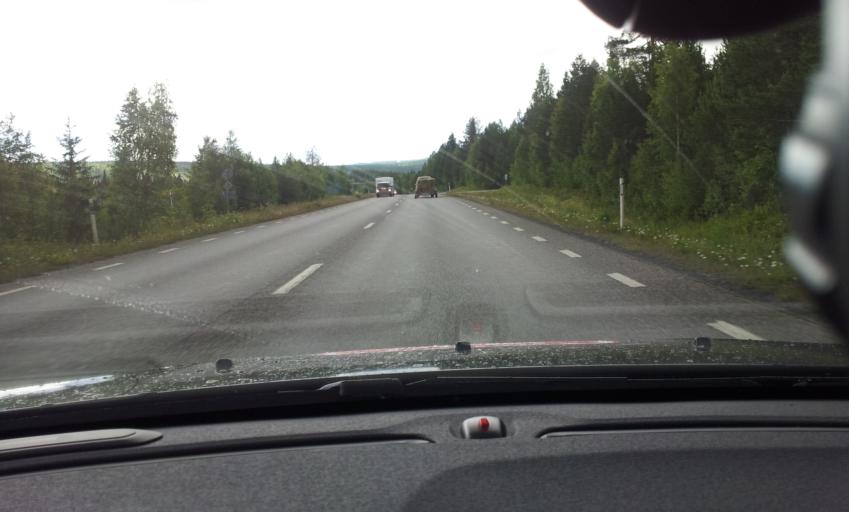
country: SE
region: Jaemtland
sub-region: Krokoms Kommun
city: Valla
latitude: 63.3113
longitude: 13.7800
